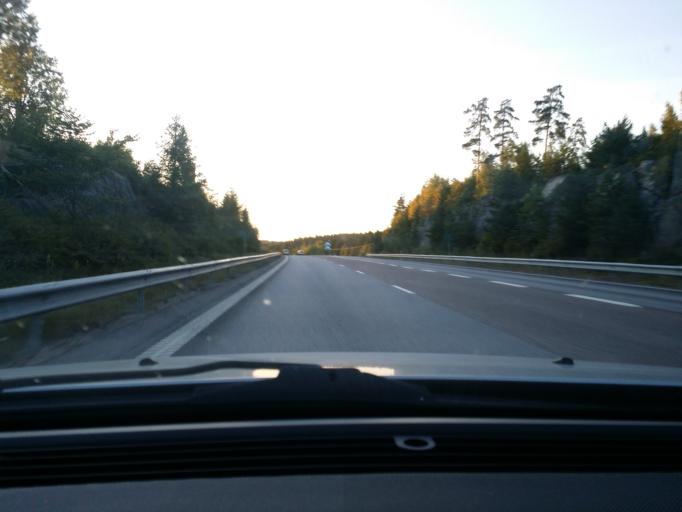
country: SE
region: Uppsala
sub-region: Enkopings Kommun
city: Dalby
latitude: 59.6190
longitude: 17.4011
